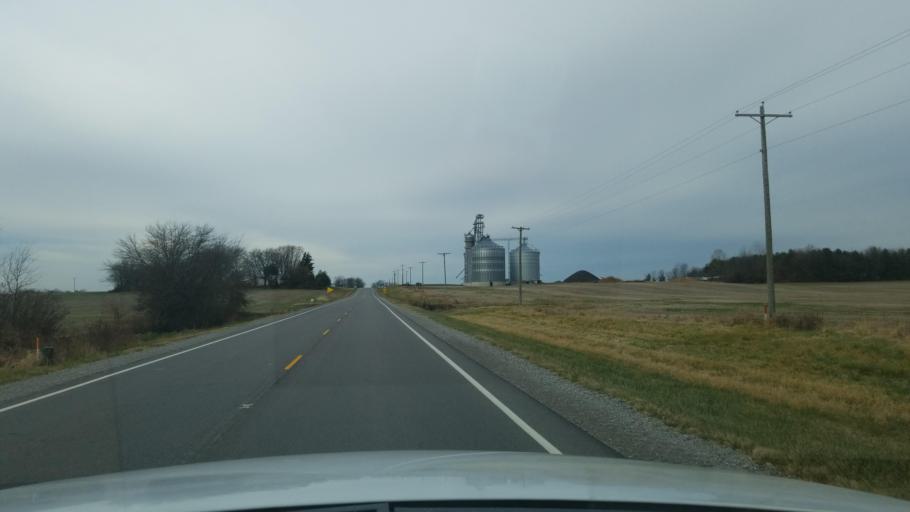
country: US
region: Illinois
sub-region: White County
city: Carmi
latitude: 37.9077
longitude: -88.1487
